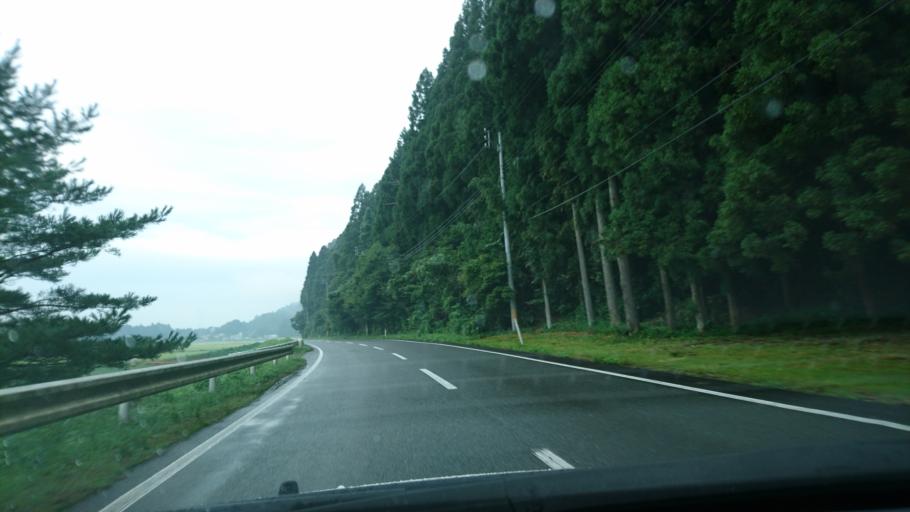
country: JP
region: Iwate
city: Ichinoseki
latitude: 38.8708
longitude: 141.2651
